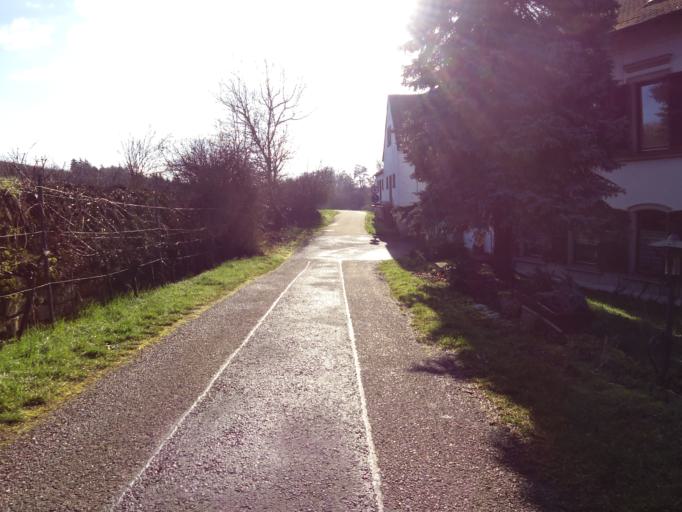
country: DE
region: Rheinland-Pfalz
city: Bissersheim
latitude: 49.5408
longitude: 8.1933
